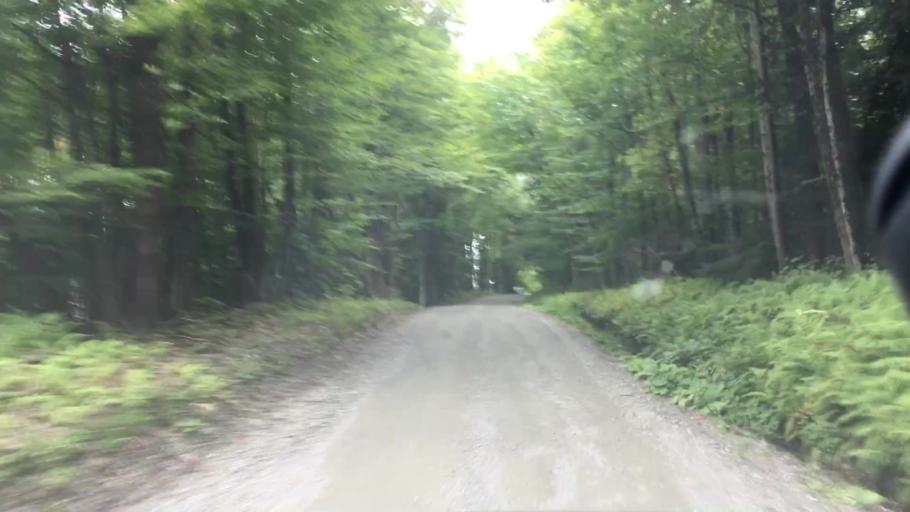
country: US
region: Vermont
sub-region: Windham County
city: Dover
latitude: 42.8408
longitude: -72.7675
